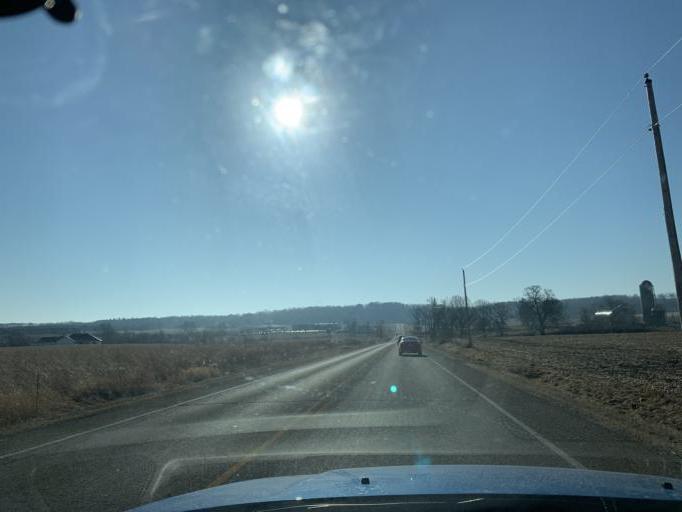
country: US
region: Wisconsin
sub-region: Dane County
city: Belleville
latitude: 42.8708
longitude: -89.5600
